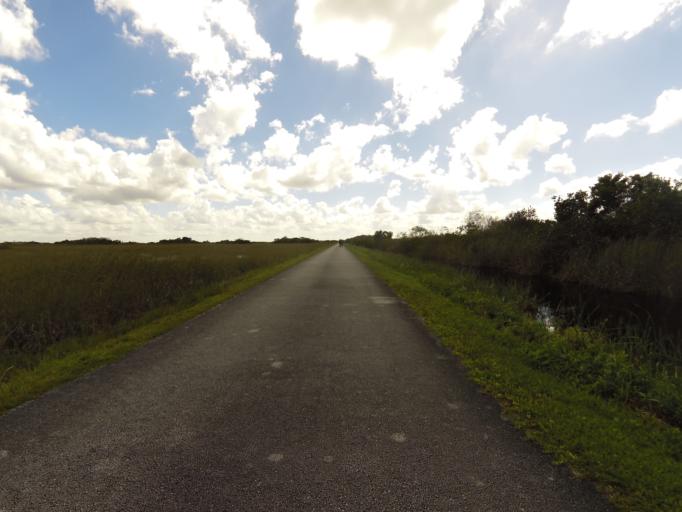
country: US
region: Florida
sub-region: Miami-Dade County
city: The Hammocks
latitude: 25.7208
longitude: -80.7667
